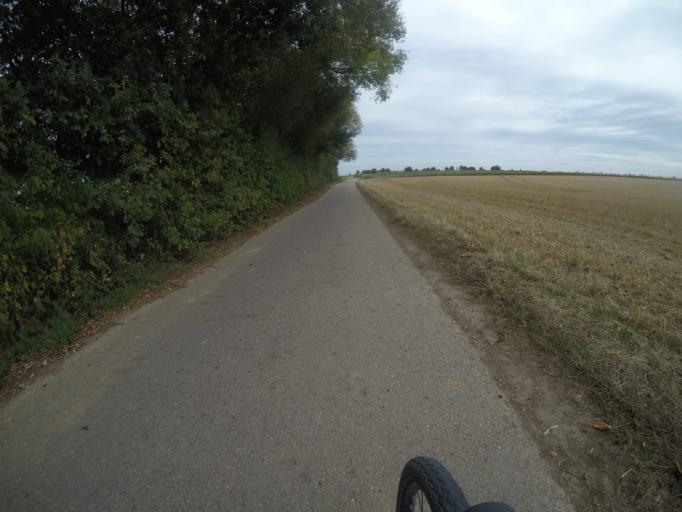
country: DE
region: Baden-Wuerttemberg
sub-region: Regierungsbezirk Stuttgart
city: Sersheim
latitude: 48.9476
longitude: 8.9934
